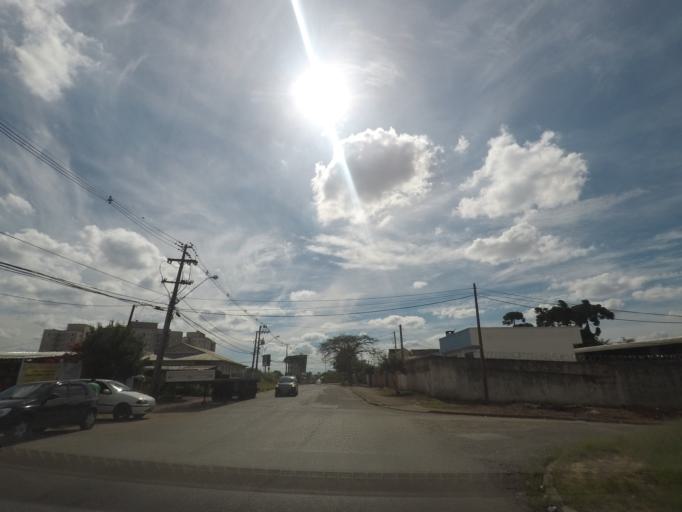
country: BR
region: Parana
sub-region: Curitiba
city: Curitiba
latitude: -25.4930
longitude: -49.2711
